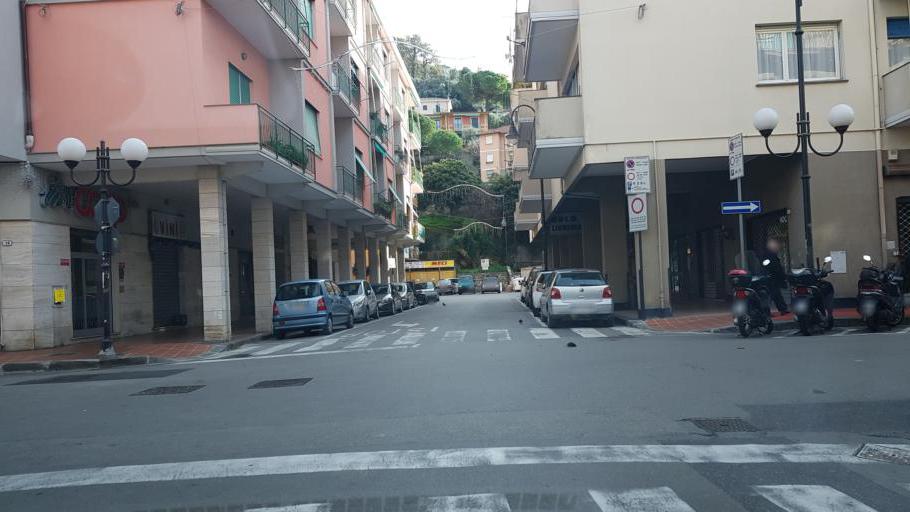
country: IT
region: Liguria
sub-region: Provincia di Genova
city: Recco
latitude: 44.3628
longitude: 9.1456
